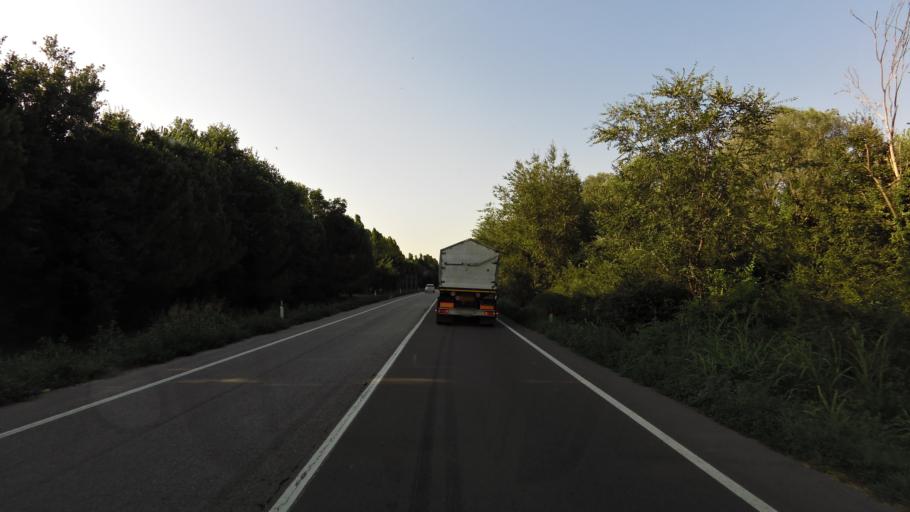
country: IT
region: Emilia-Romagna
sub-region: Provincia di Ravenna
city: Ravenna
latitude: 44.4727
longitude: 12.2095
